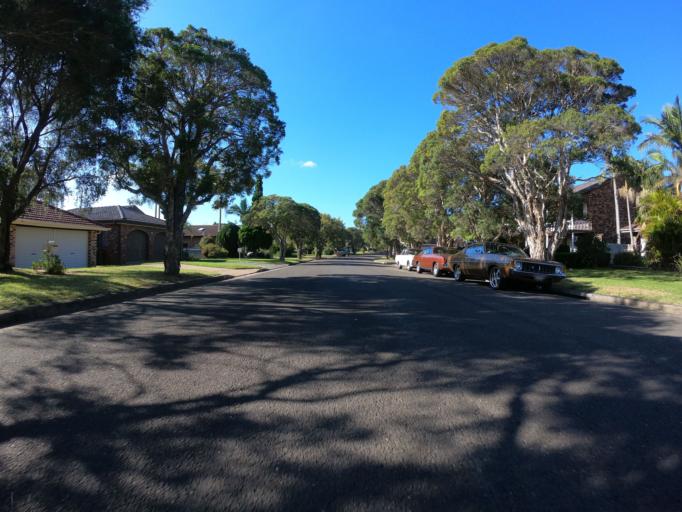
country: AU
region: New South Wales
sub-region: Wollongong
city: Cordeaux Heights
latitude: -34.4403
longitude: 150.8492
